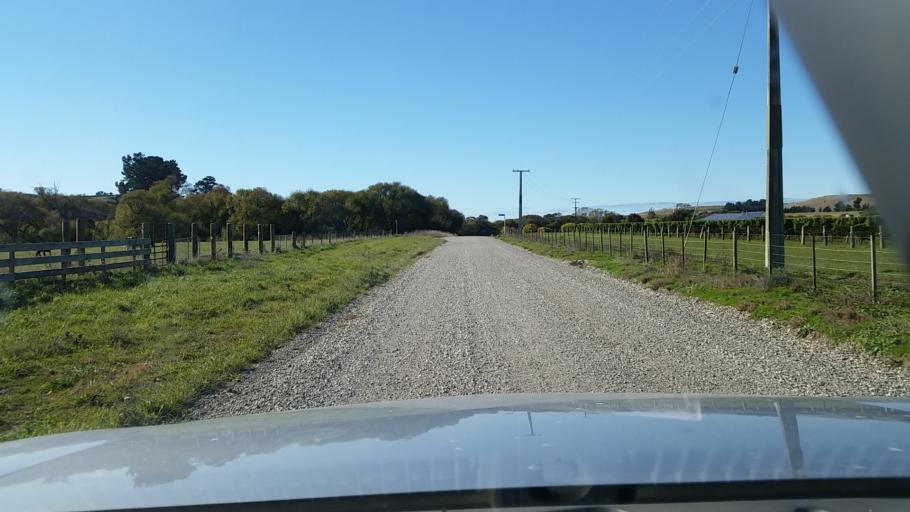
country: NZ
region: Marlborough
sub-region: Marlborough District
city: Blenheim
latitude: -41.6808
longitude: 174.1338
